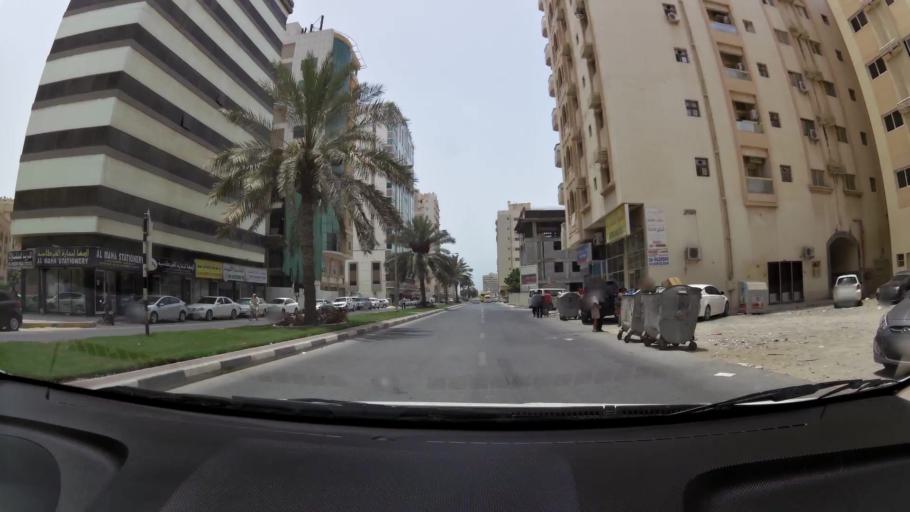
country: AE
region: Ash Shariqah
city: Sharjah
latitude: 25.3546
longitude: 55.3941
